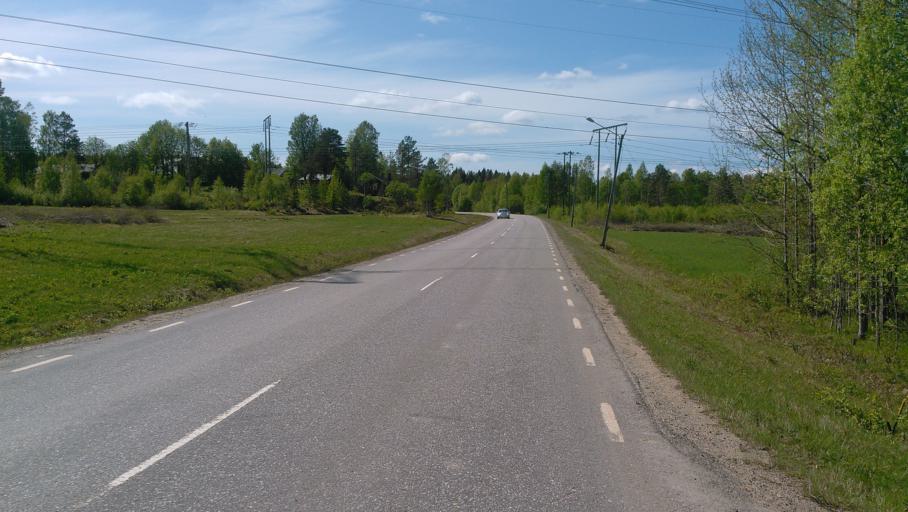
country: SE
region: Vaesterbotten
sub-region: Umea Kommun
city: Roback
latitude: 63.8639
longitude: 20.0158
